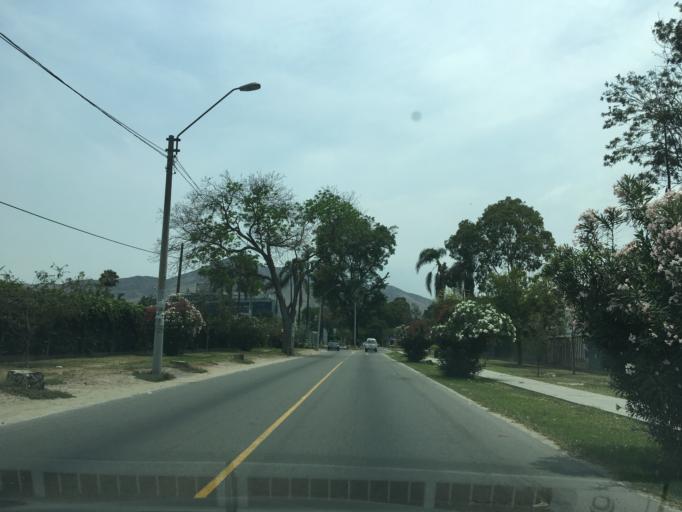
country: PE
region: Lima
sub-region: Lima
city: La Molina
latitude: -12.0787
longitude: -76.9479
